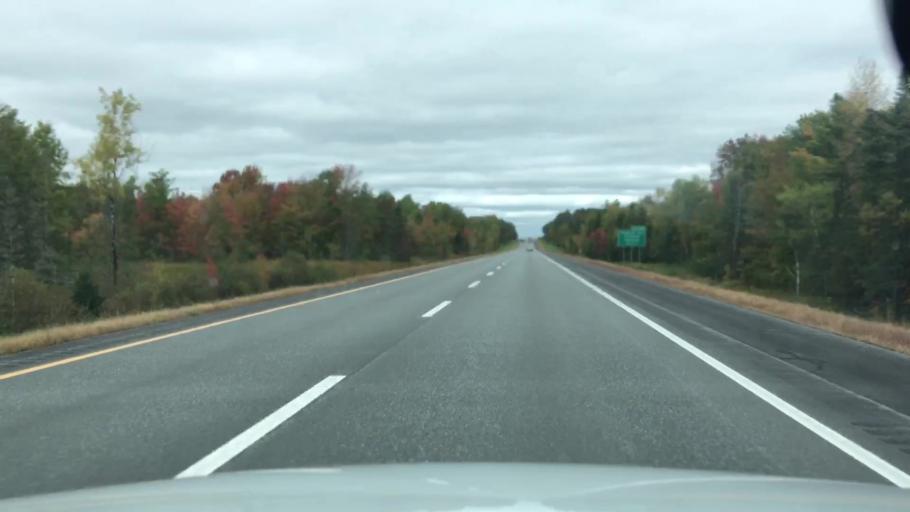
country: US
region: Maine
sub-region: Somerset County
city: Pittsfield
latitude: 44.7534
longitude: -69.4204
